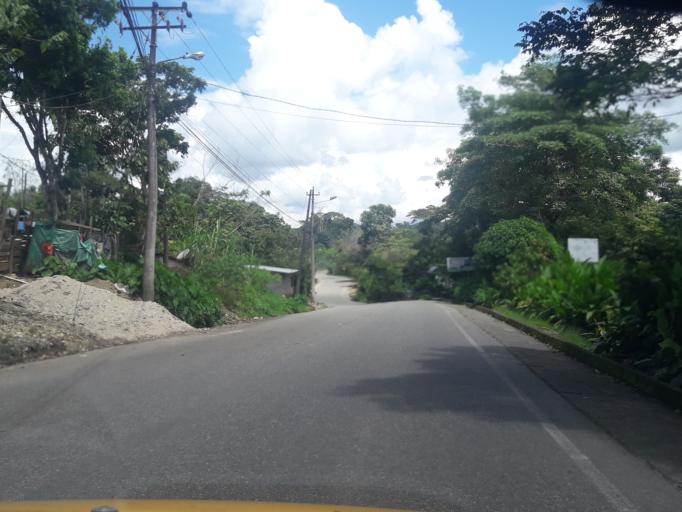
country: EC
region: Napo
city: Tena
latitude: -1.0083
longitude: -77.8206
